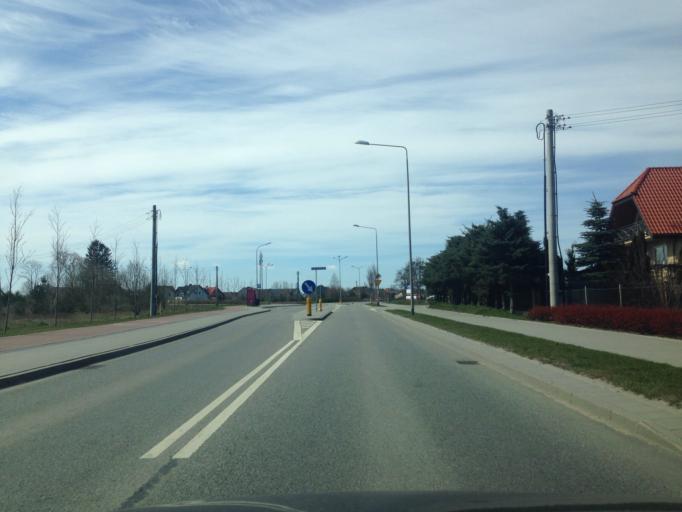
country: PL
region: Pomeranian Voivodeship
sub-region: Powiat kartuski
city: Chwaszczyno
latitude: 54.4989
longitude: 18.4355
